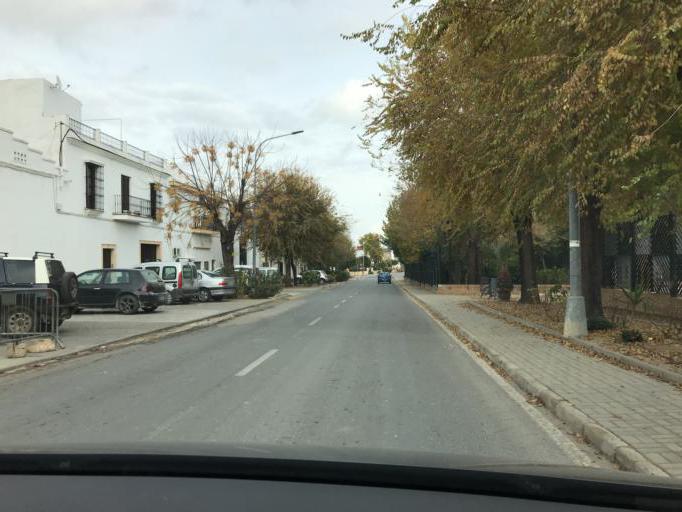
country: ES
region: Andalusia
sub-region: Provincia de Sevilla
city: La Lantejuela
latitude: 37.3556
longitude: -5.2237
